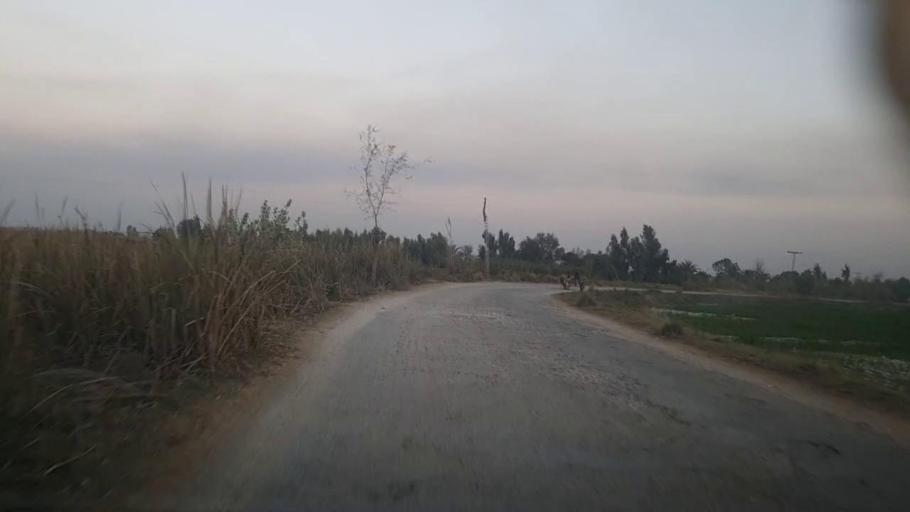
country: PK
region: Sindh
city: Kandiari
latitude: 26.6815
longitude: 68.9420
